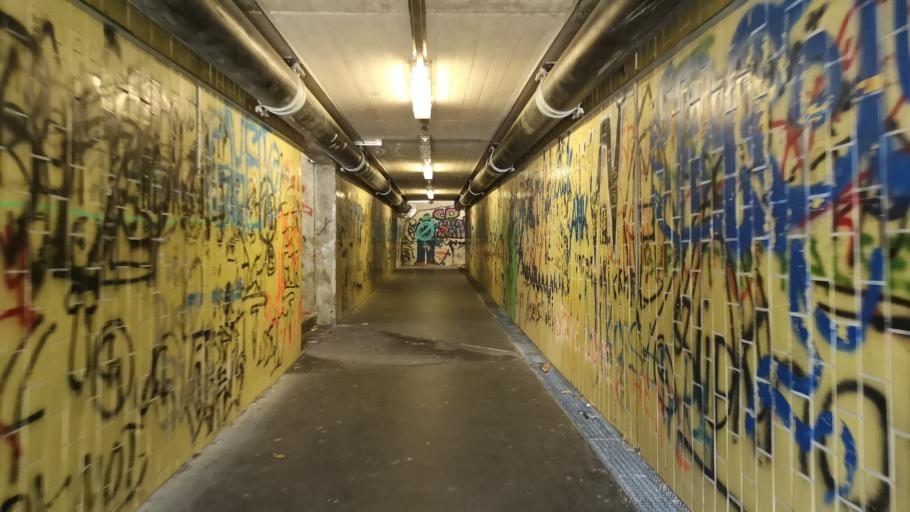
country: AT
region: Styria
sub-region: Politischer Bezirk Deutschlandsberg
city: Deutschlandsberg
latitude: 46.8189
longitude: 15.2177
